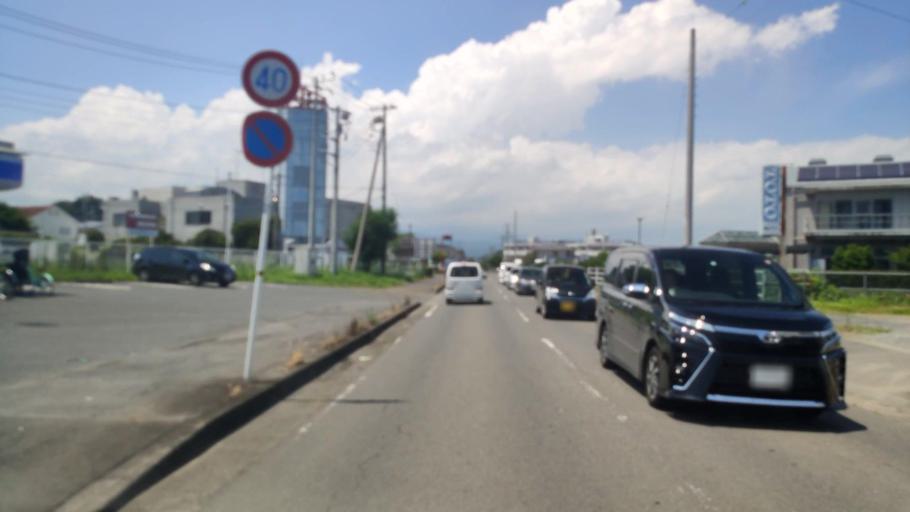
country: JP
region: Kanagawa
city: Oiso
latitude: 35.3446
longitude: 139.3058
